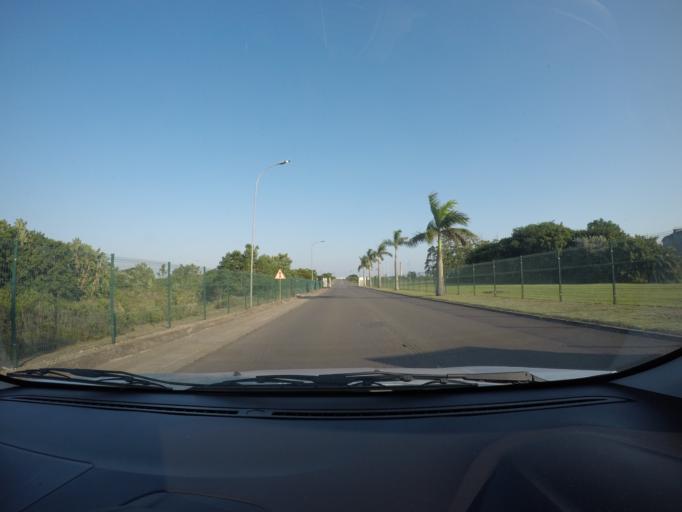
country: ZA
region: KwaZulu-Natal
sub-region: uThungulu District Municipality
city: Richards Bay
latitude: -28.7648
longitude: 31.9984
